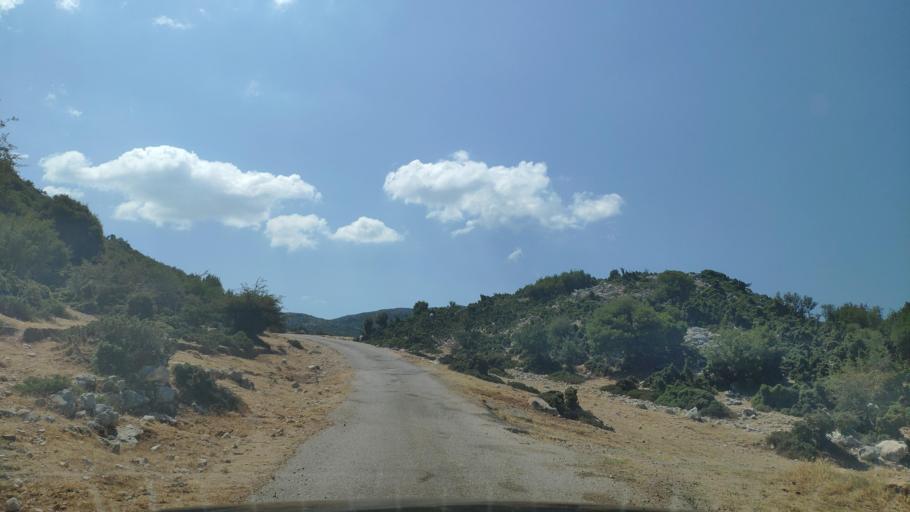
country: GR
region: West Greece
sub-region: Nomos Aitolias kai Akarnanias
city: Monastirakion
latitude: 38.8029
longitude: 20.9472
